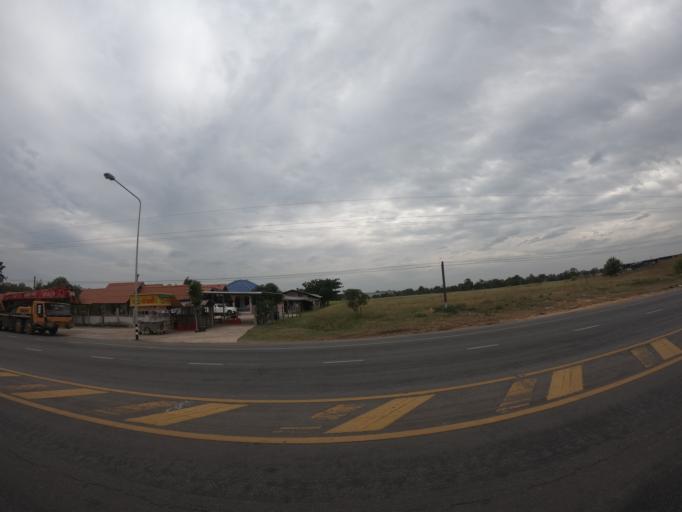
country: TH
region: Roi Et
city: Thawat Buri
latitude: 16.0820
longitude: 103.7089
